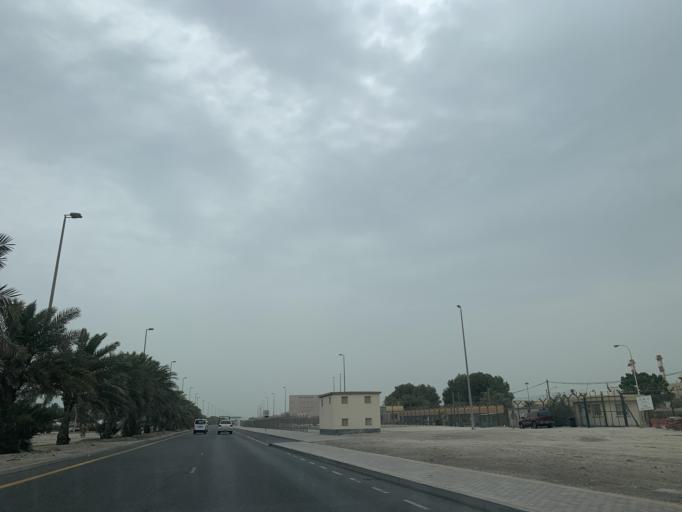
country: BH
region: Muharraq
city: Al Hadd
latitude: 26.2250
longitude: 50.6603
